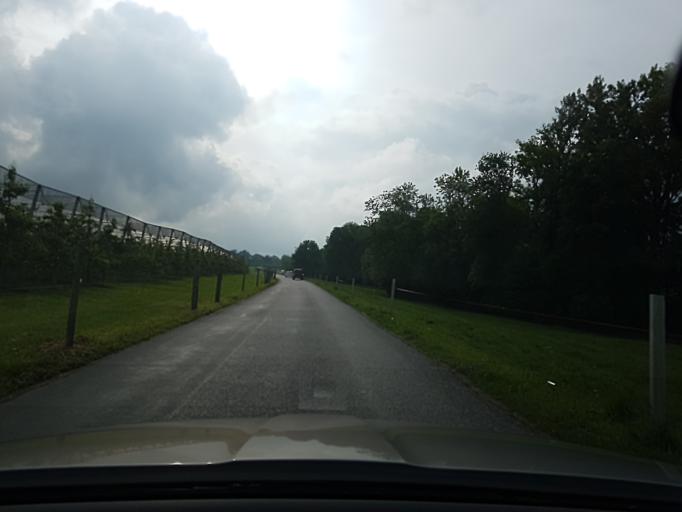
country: CH
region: Thurgau
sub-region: Arbon District
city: Egnach
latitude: 47.5145
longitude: 9.3682
